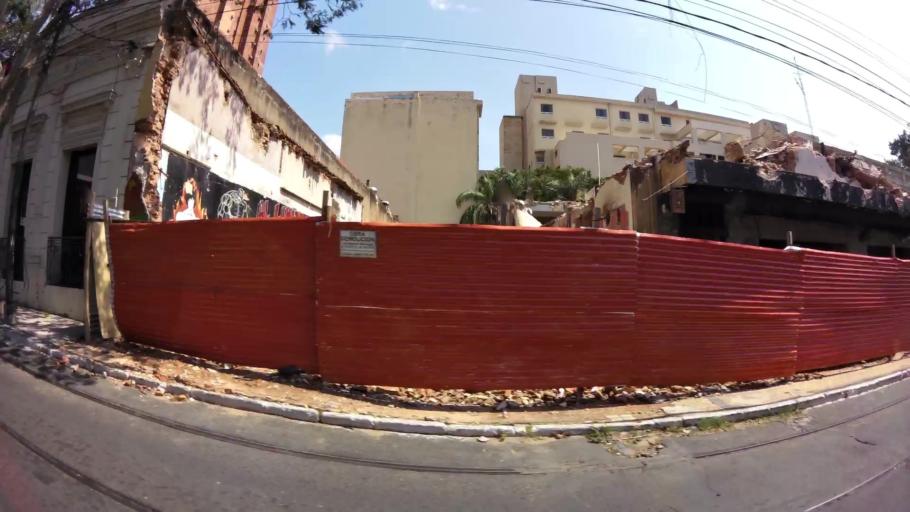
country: PY
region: Asuncion
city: Asuncion
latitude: -25.2874
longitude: -57.6272
